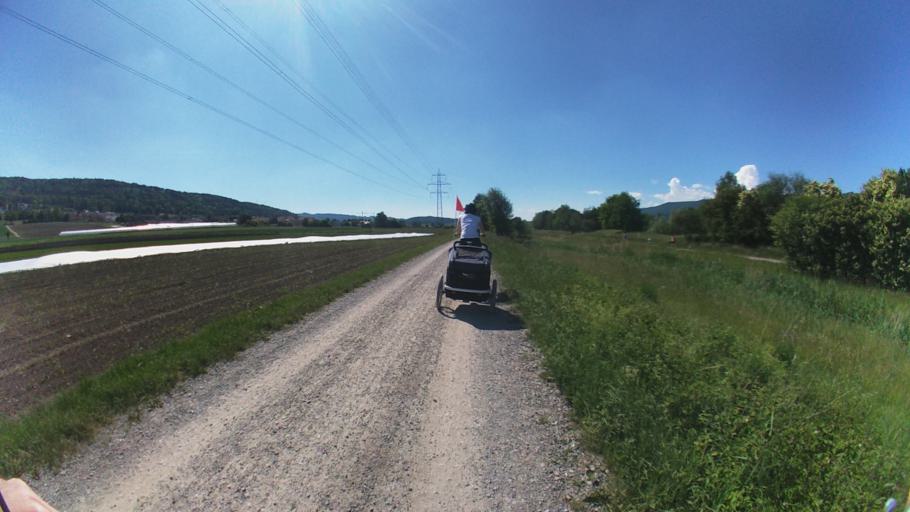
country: CH
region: Zurich
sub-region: Bezirk Dielsdorf
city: Daenikon
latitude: 47.4501
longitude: 8.4147
